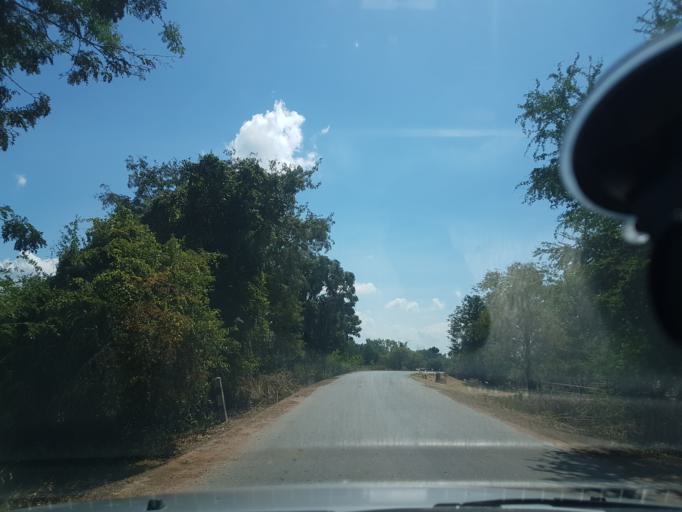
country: TH
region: Lop Buri
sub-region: Amphoe Tha Luang
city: Tha Luang
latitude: 14.9991
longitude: 101.0108
